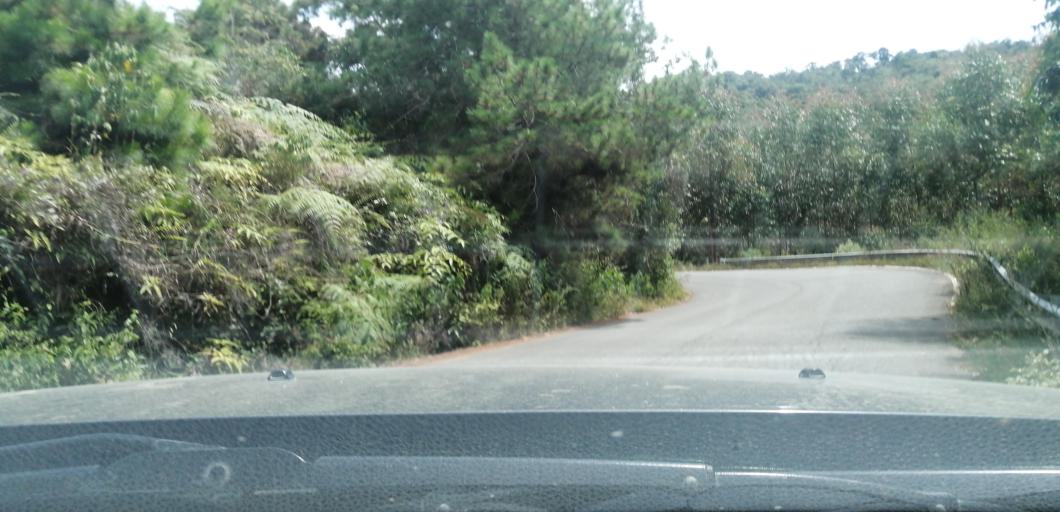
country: CO
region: Valle del Cauca
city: Dagua
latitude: 3.7109
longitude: -76.5850
